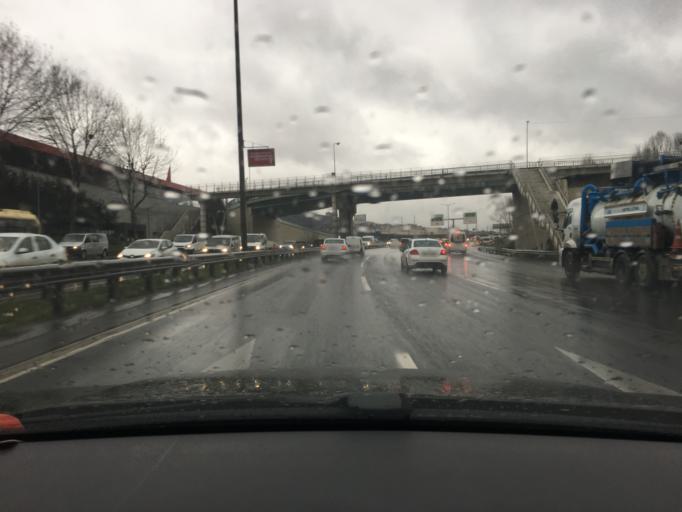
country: TR
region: Istanbul
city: Esenler
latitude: 41.0374
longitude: 28.8897
